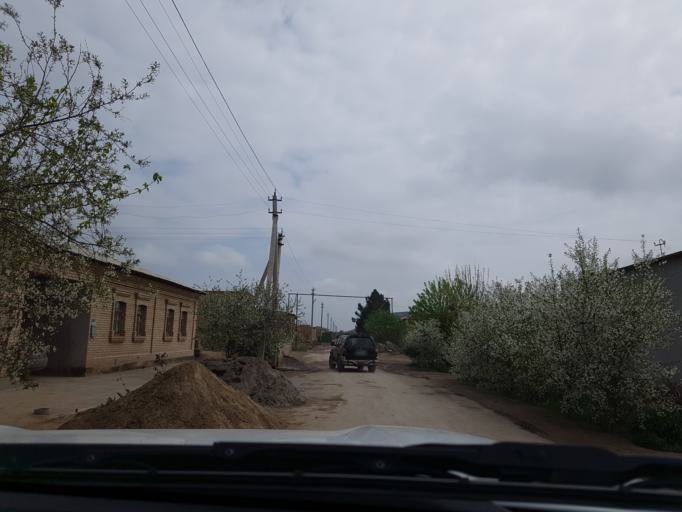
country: TM
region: Lebap
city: Turkmenabat
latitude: 38.9712
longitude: 63.6923
